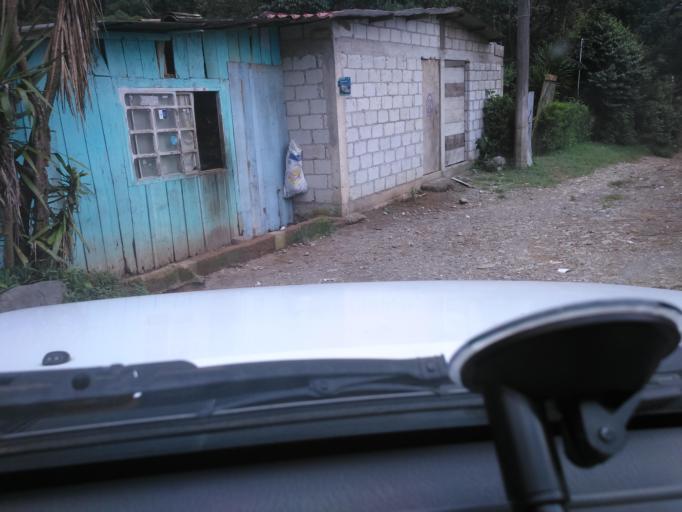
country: MX
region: Veracruz
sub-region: Mariano Escobedo
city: Chicola
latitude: 18.9121
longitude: -97.1101
